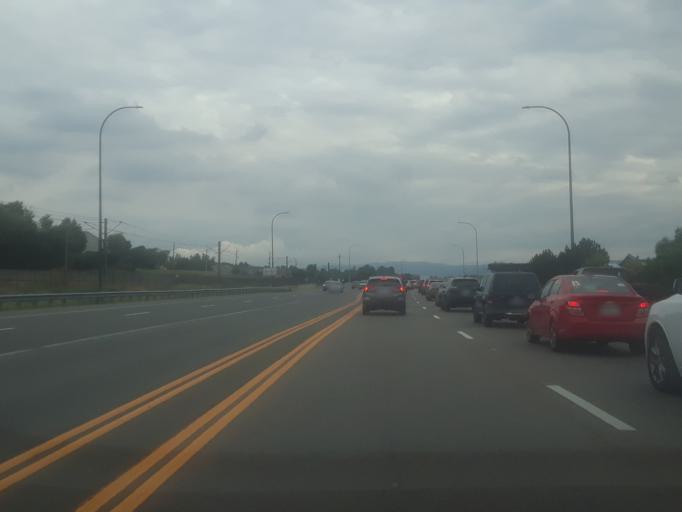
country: US
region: Colorado
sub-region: Arapahoe County
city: Columbine Valley
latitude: 39.5843
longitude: -105.0236
